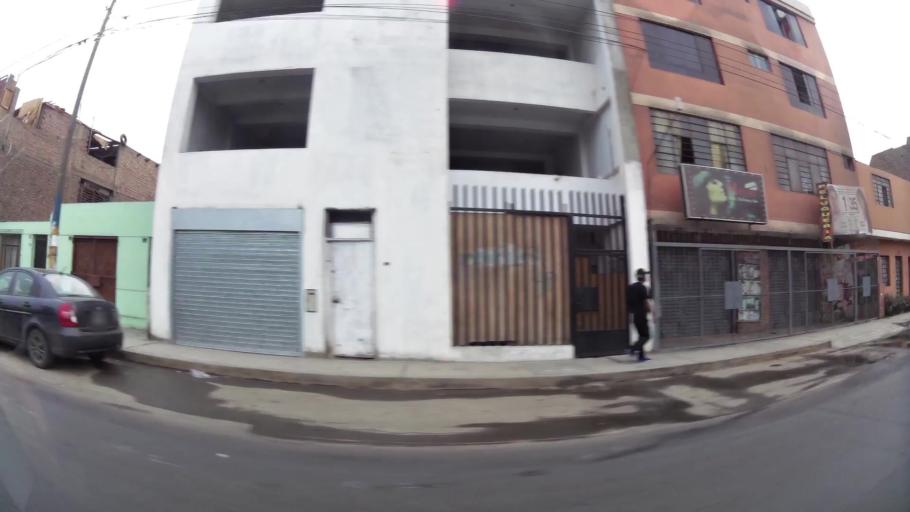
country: PE
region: Lima
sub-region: Lima
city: Independencia
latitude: -12.0023
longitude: -77.0130
